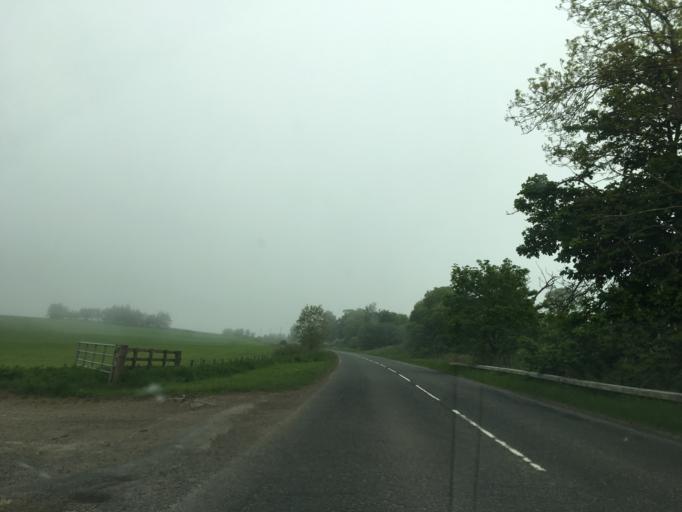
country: GB
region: Scotland
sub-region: The Scottish Borders
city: West Linton
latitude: 55.7382
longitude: -3.3009
